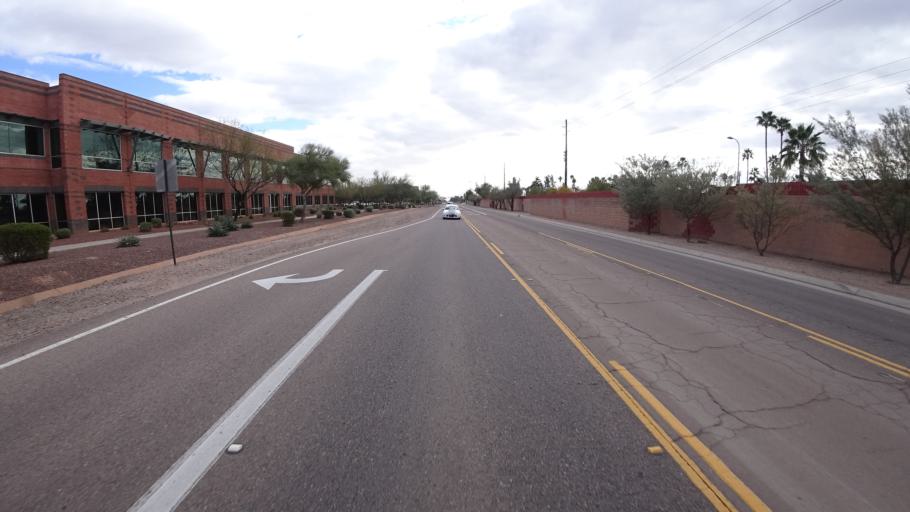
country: US
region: Arizona
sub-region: Maricopa County
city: Scottsdale
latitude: 33.5126
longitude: -111.8915
